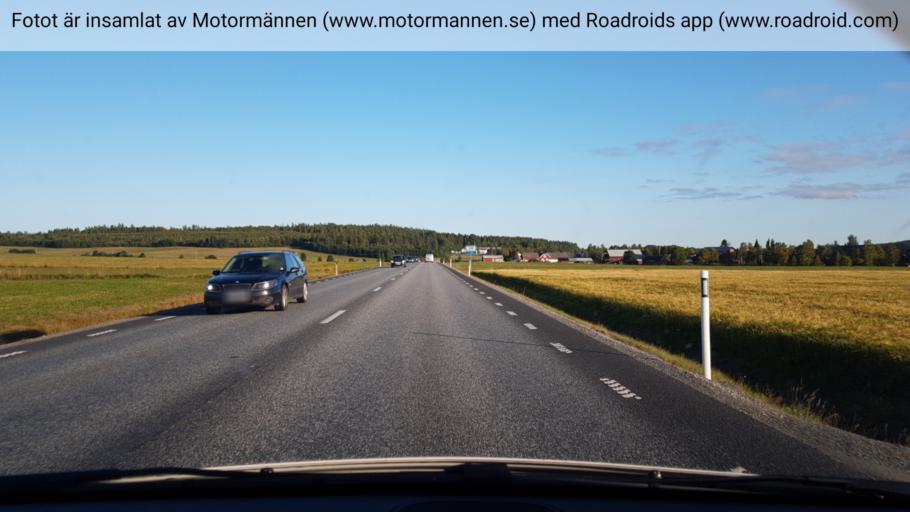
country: SE
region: Vaesterbotten
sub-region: Umea Kommun
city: Roback
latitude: 63.8699
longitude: 20.0753
